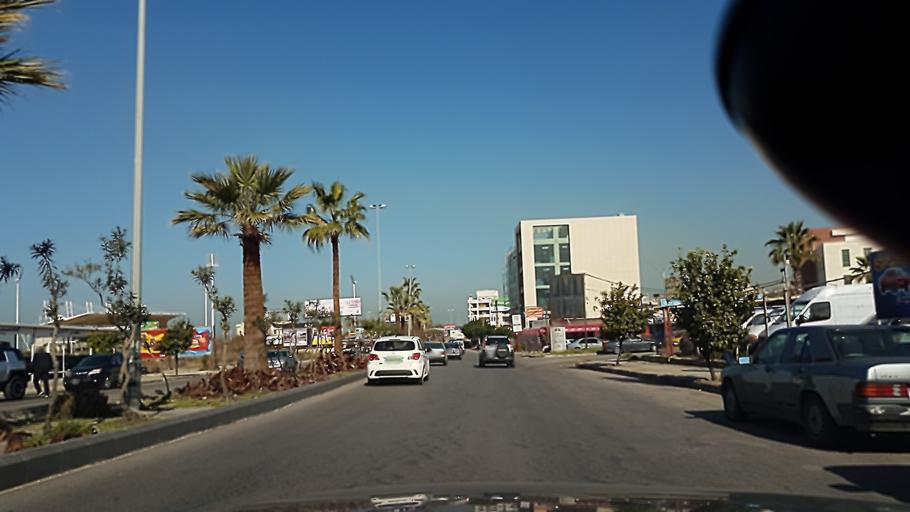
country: LB
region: Liban-Sud
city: Sidon
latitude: 33.5812
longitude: 35.3868
